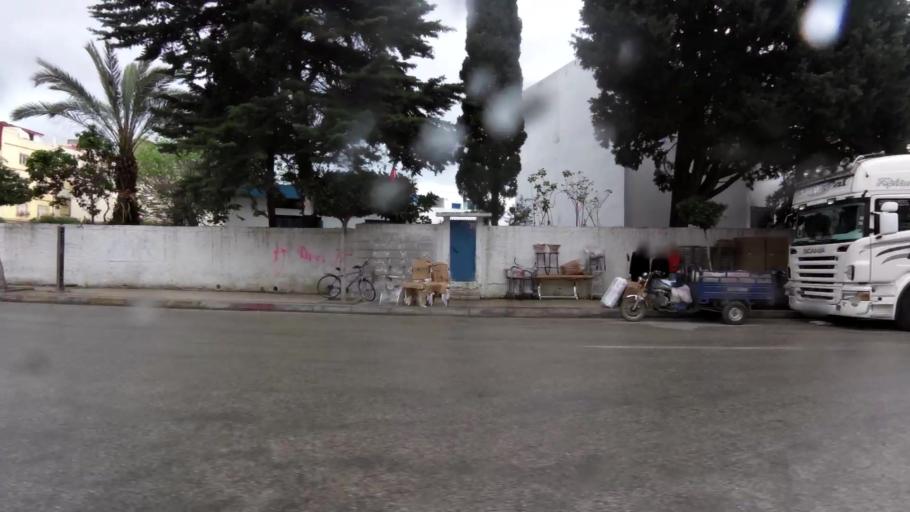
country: MA
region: Tanger-Tetouan
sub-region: Tanger-Assilah
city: Tangier
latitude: 35.7618
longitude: -5.8233
